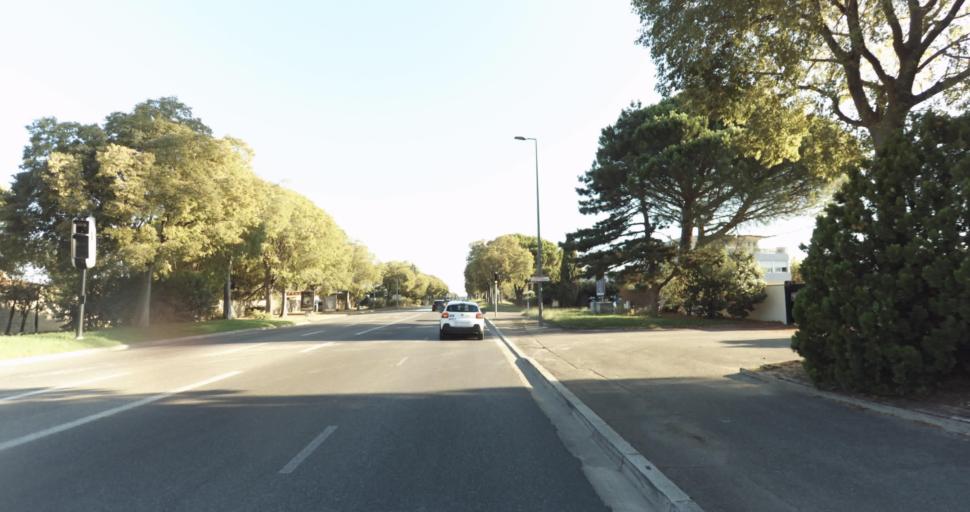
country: FR
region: Provence-Alpes-Cote d'Azur
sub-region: Departement des Bouches-du-Rhone
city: Miramas
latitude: 43.5920
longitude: 5.0040
